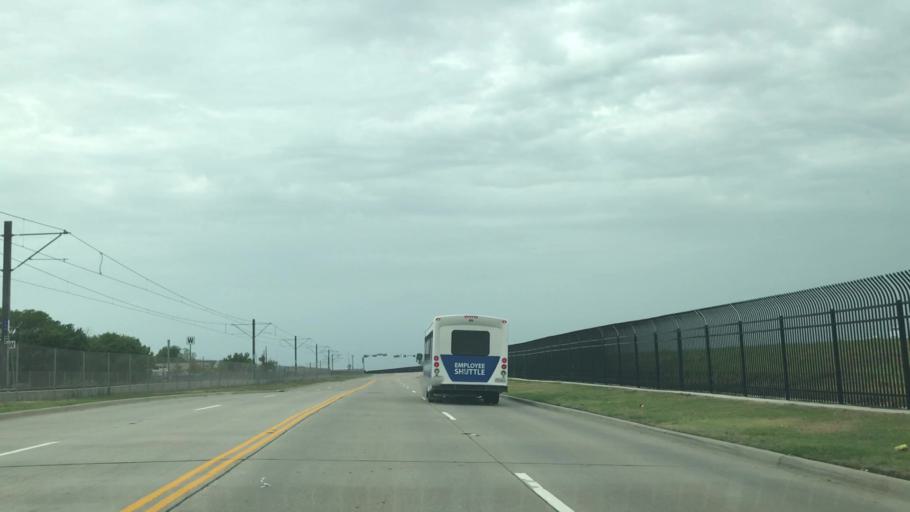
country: US
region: Texas
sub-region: Dallas County
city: University Park
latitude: 32.8354
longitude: -96.8476
